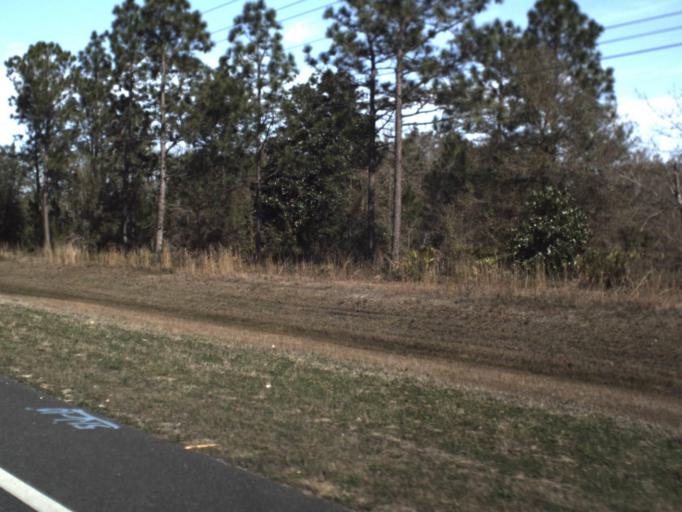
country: US
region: Florida
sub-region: Bay County
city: Lynn Haven
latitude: 30.3049
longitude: -85.6494
